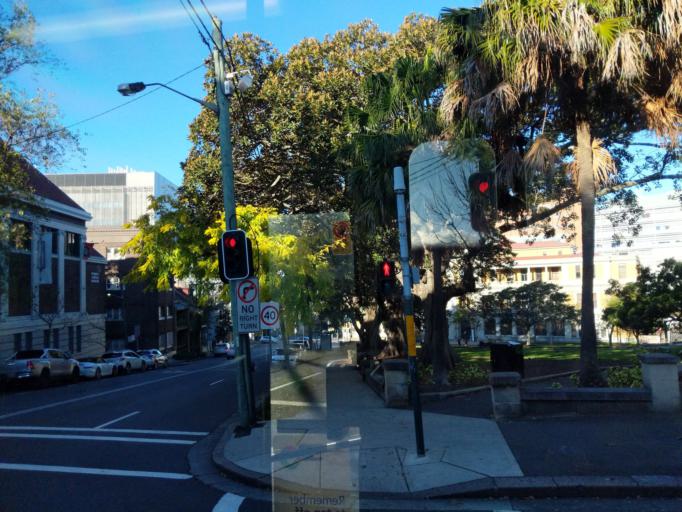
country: AU
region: New South Wales
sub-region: City of Sydney
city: Darlinghurst
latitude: -33.8792
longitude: 151.2199
